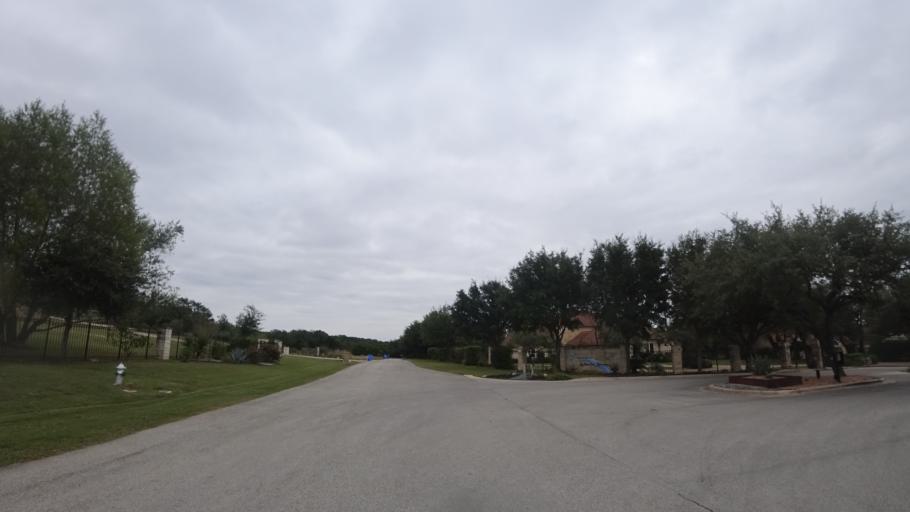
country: US
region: Texas
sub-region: Travis County
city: Lakeway
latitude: 30.3699
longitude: -97.9414
